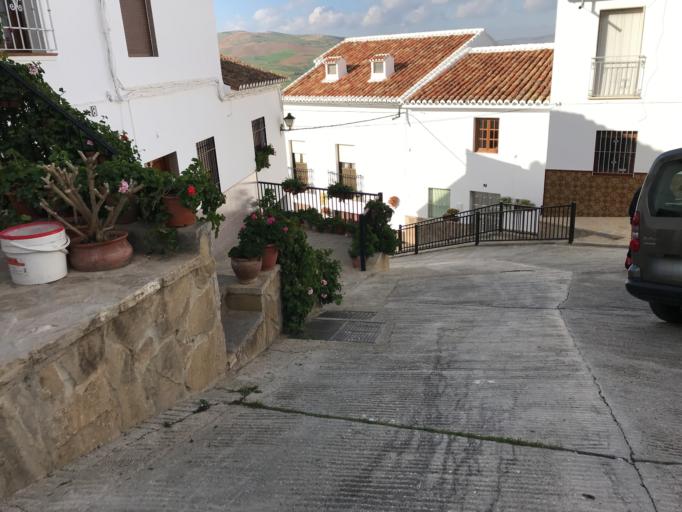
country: ES
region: Andalusia
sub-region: Provincia de Malaga
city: Ardales
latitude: 36.8771
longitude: -4.8458
